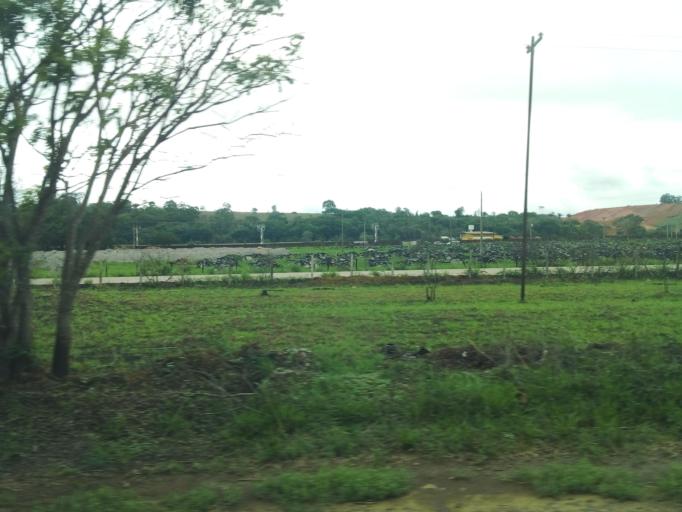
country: BR
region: Minas Gerais
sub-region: Ipatinga
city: Ipatinga
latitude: -19.4745
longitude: -42.4850
